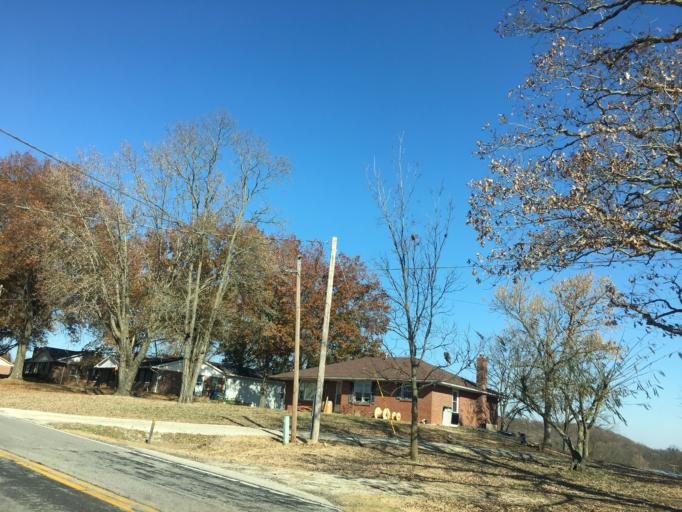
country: US
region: Missouri
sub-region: Cole County
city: Wardsville
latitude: 38.4662
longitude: -92.1752
